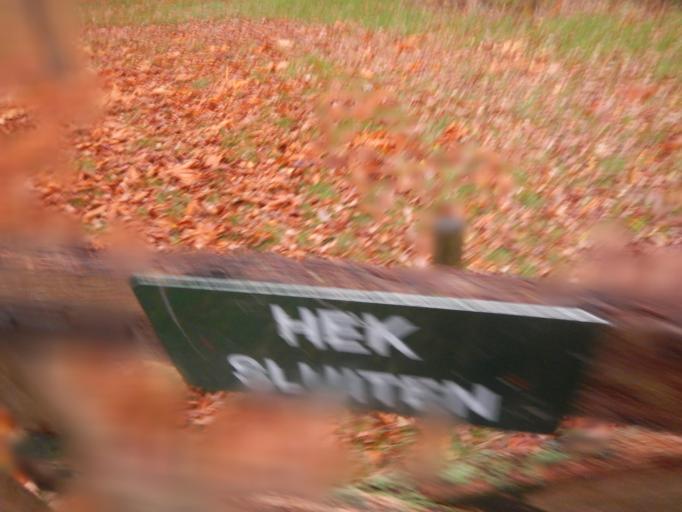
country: NL
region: Gelderland
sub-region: Gemeente Barneveld
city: Garderen
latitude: 52.2732
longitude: 5.7230
